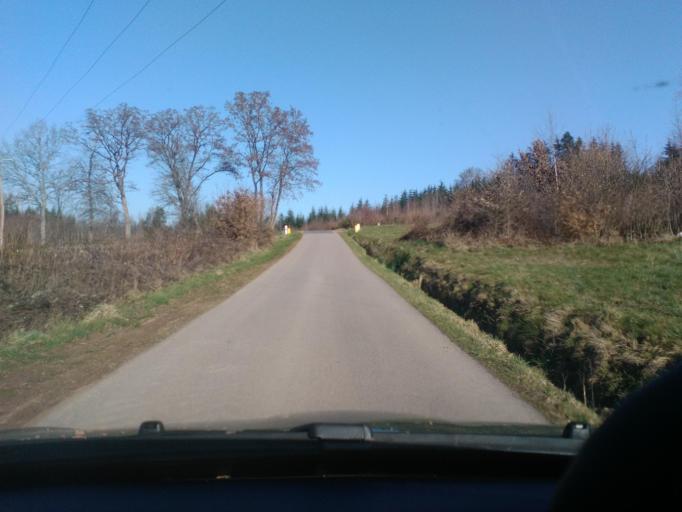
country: FR
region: Lorraine
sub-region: Departement des Vosges
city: Moyenmoutier
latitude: 48.3626
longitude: 6.9184
